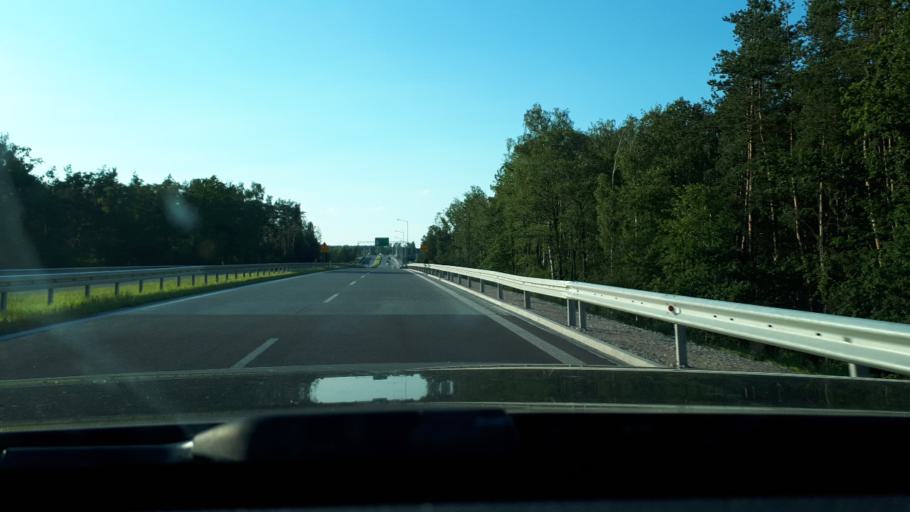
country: PL
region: Masovian Voivodeship
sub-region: Powiat piaseczynski
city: Baniocha
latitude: 51.9945
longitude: 21.1703
